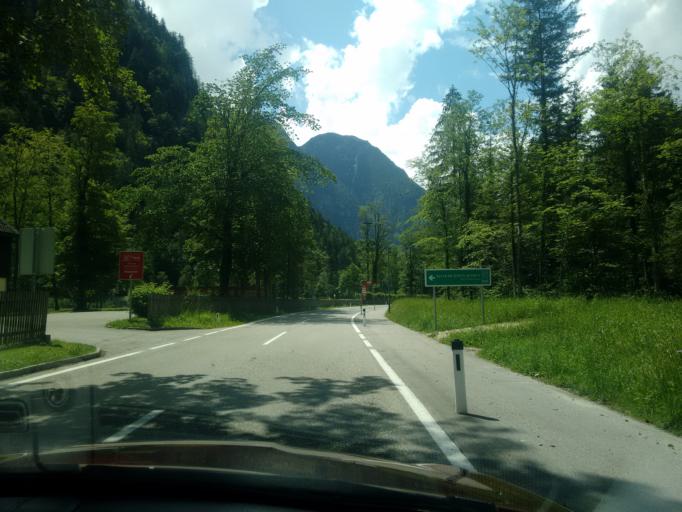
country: AT
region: Styria
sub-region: Politischer Bezirk Liezen
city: Bad Aussee
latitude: 47.5517
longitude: 13.6936
